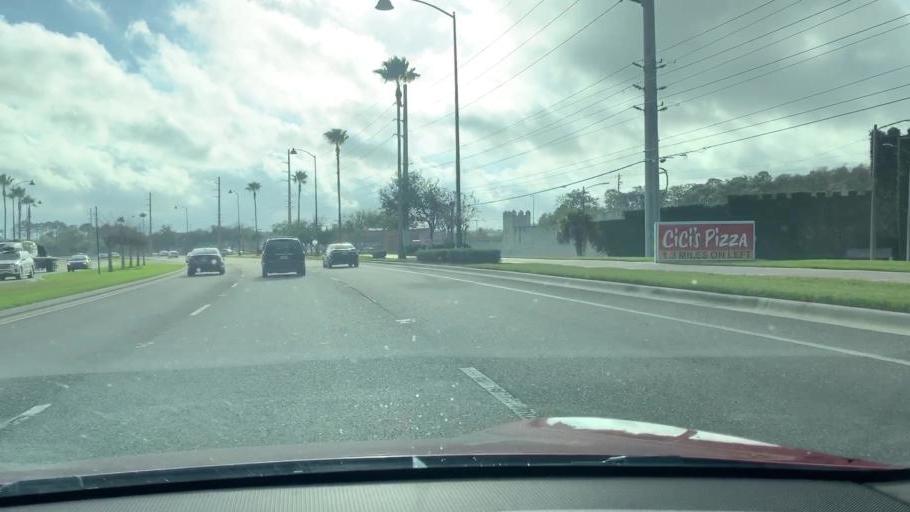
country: US
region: Florida
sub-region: Osceola County
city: Kissimmee
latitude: 28.3049
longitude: -81.4622
